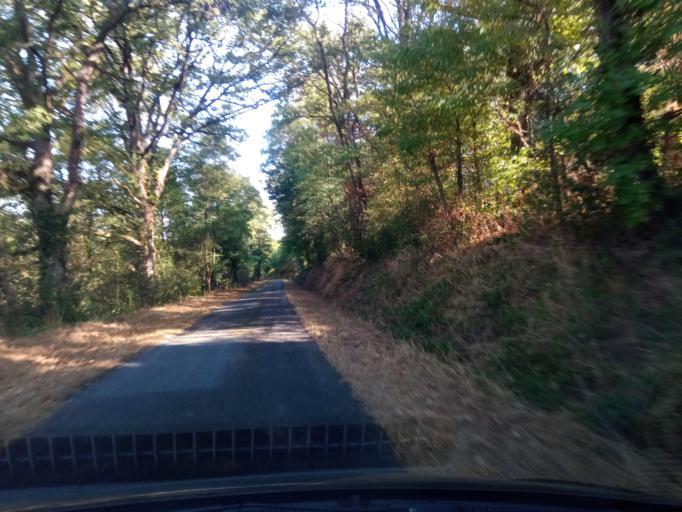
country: FR
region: Poitou-Charentes
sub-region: Departement de la Vienne
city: Saulge
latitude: 46.3747
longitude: 0.8718
